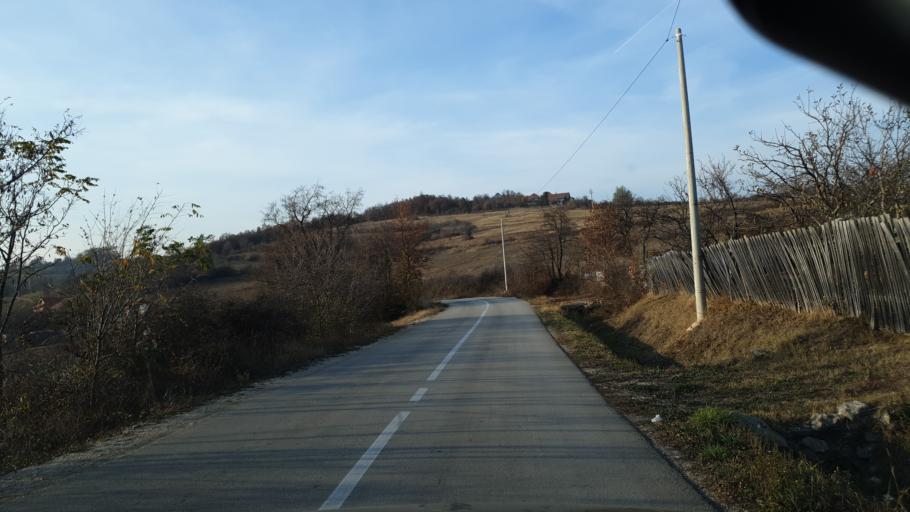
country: RS
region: Central Serbia
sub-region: Borski Okrug
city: Bor
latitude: 44.0483
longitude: 22.0925
